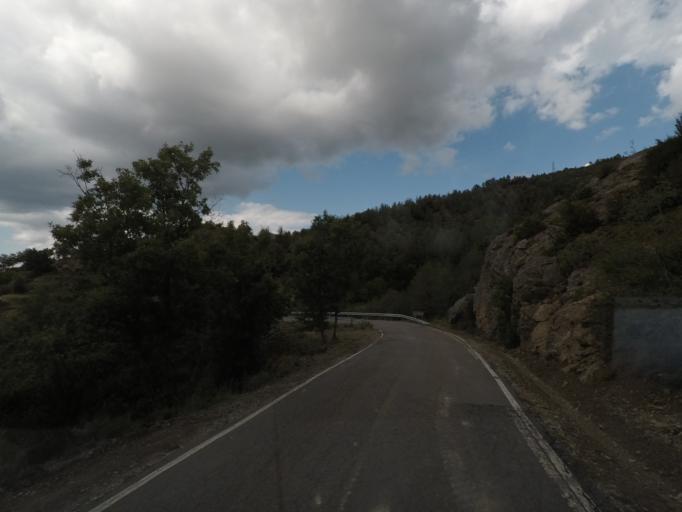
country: ES
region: Aragon
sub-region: Provincia de Huesca
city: Fiscal
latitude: 42.4096
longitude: -0.1092
